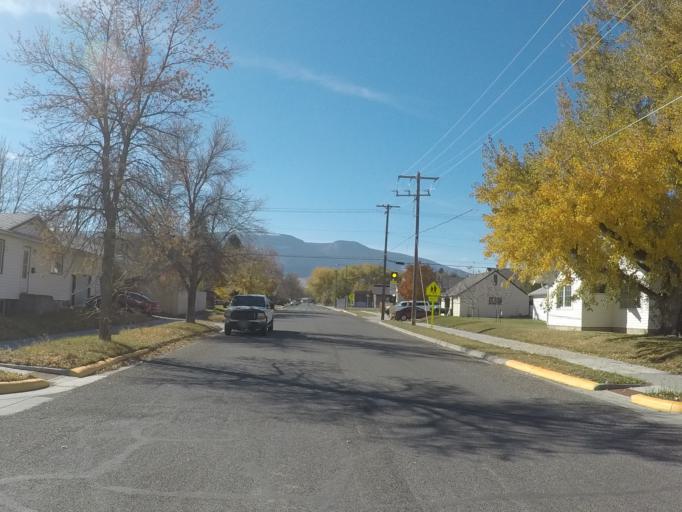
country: US
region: Montana
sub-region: Park County
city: Livingston
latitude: 45.6535
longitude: -110.5658
